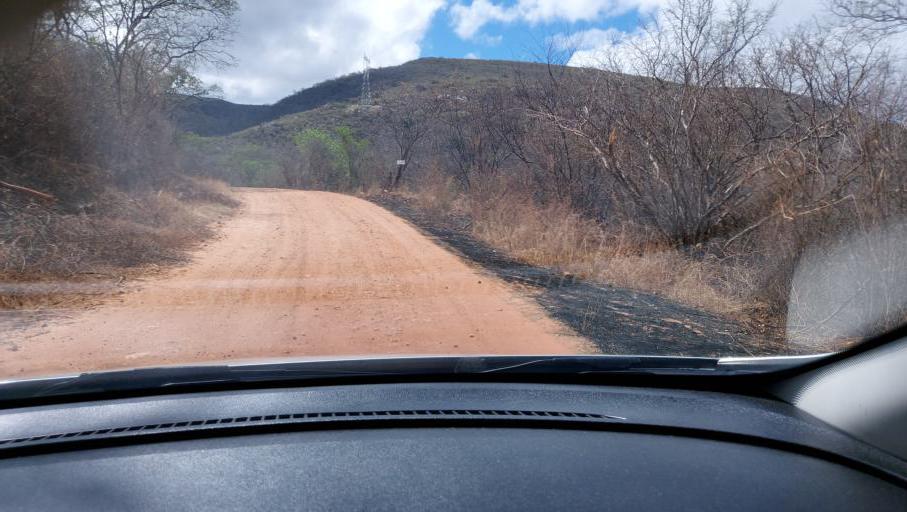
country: BR
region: Bahia
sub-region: Oliveira Dos Brejinhos
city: Beira Rio
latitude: -12.0979
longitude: -42.5507
